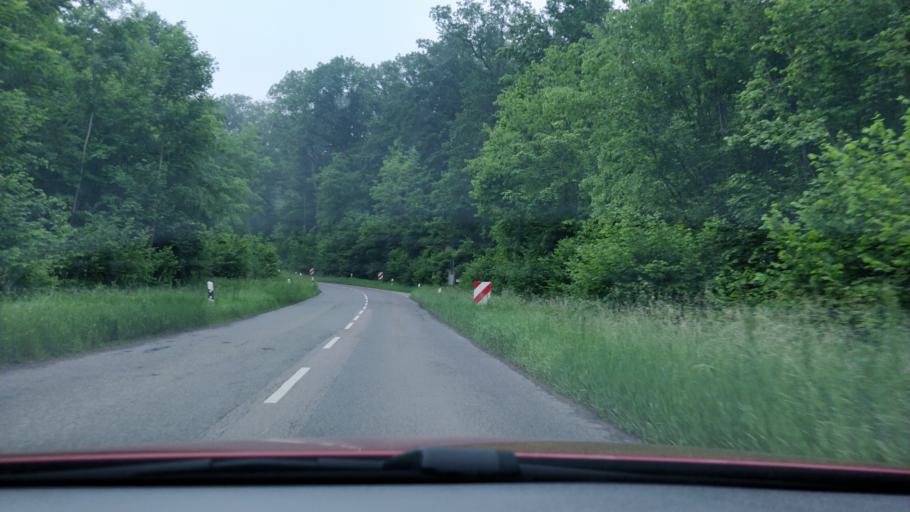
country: DE
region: Baden-Wuerttemberg
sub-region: Regierungsbezirk Stuttgart
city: Leinfelden-Echterdingen
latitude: 48.7302
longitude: 9.1730
